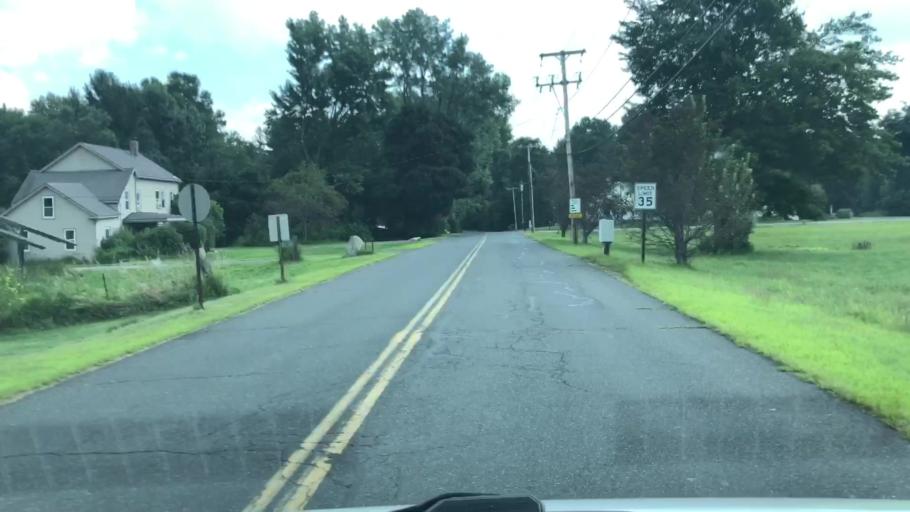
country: US
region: Massachusetts
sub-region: Hampshire County
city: Hatfield
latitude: 42.3812
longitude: -72.6288
